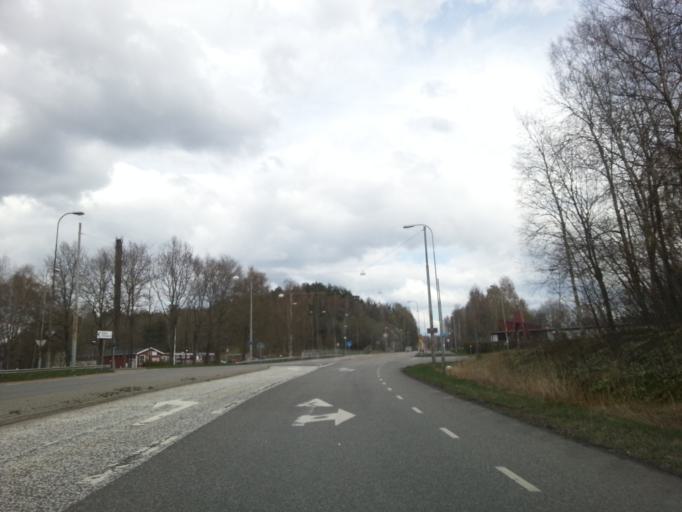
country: SE
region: Vaestra Goetaland
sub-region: Goteborg
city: Hammarkullen
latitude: 57.7813
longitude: 12.0271
